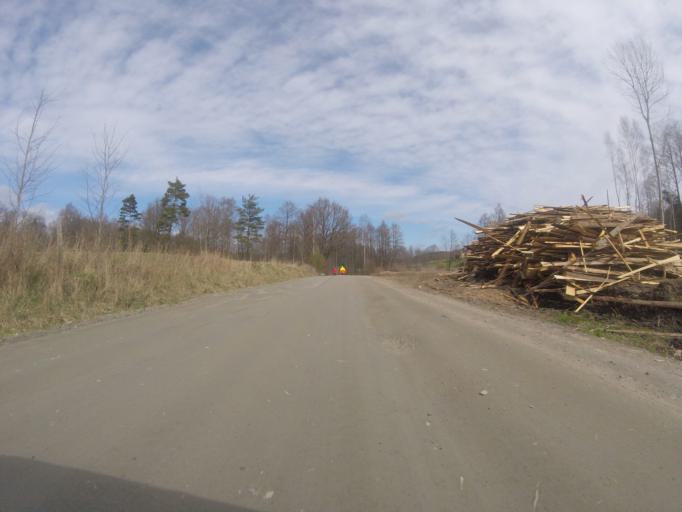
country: SE
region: Vaestra Goetaland
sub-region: Alingsas Kommun
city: Ingared
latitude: 57.8668
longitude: 12.4959
